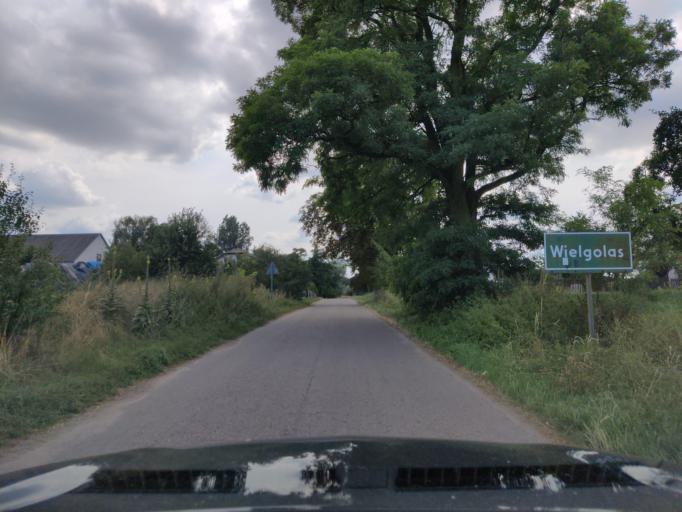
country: PL
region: Masovian Voivodeship
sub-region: Powiat pultuski
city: Obryte
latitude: 52.6900
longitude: 21.2452
